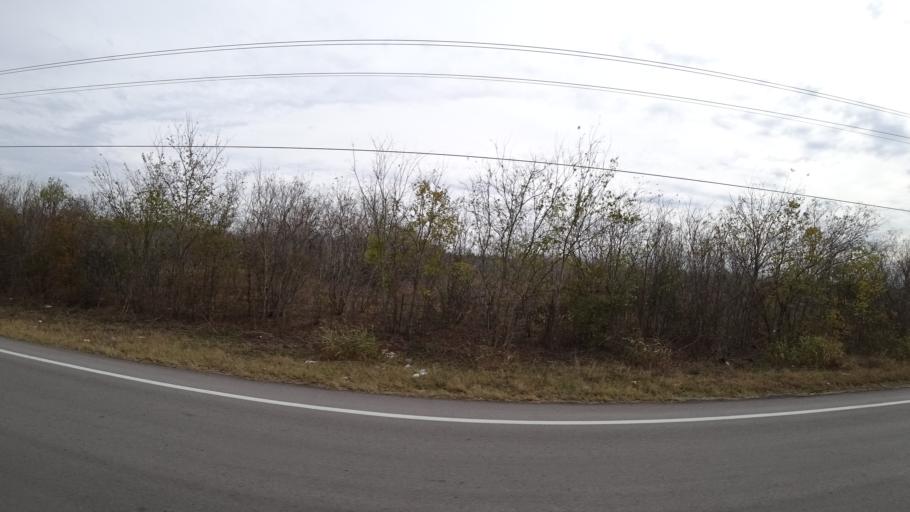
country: US
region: Texas
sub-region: Travis County
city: Garfield
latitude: 30.1449
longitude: -97.5650
